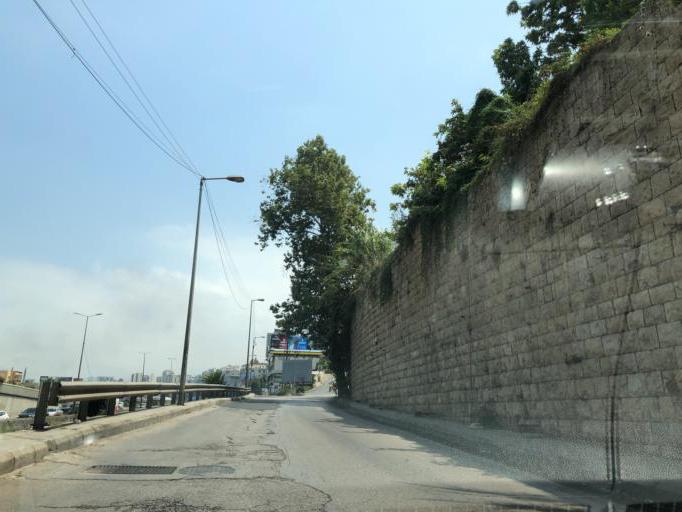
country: LB
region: Mont-Liban
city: Djounie
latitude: 33.9563
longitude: 35.5993
